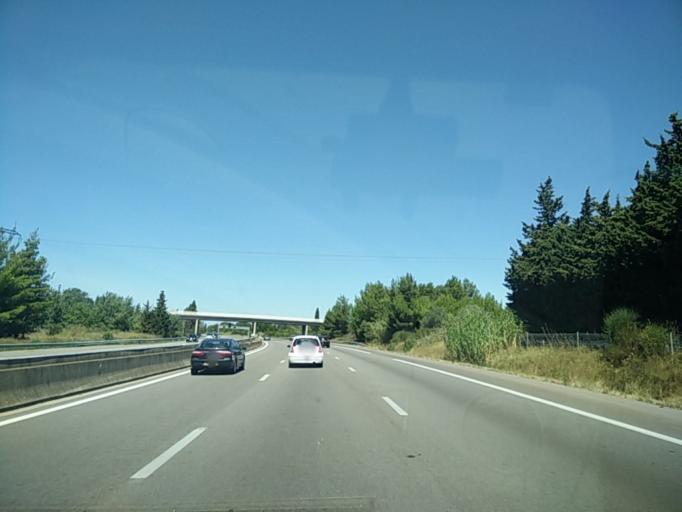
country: FR
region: Provence-Alpes-Cote d'Azur
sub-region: Departement du Vaucluse
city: Morieres-les-Avignon
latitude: 43.9462
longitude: 4.9111
